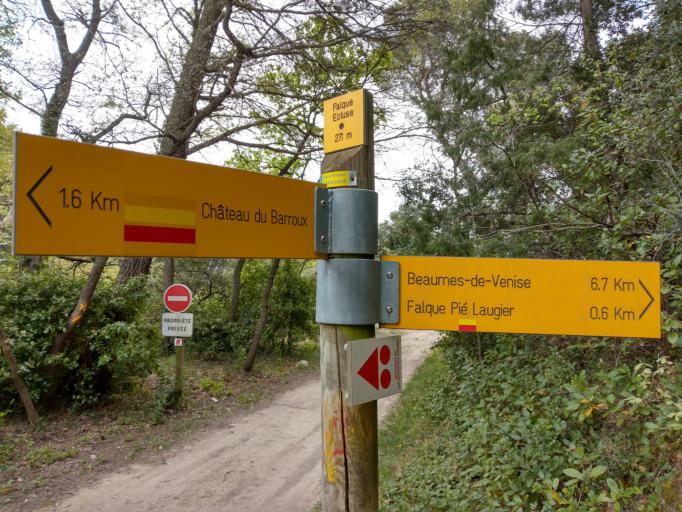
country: FR
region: Provence-Alpes-Cote d'Azur
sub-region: Departement du Vaucluse
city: Caromb
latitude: 44.1359
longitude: 5.0890
